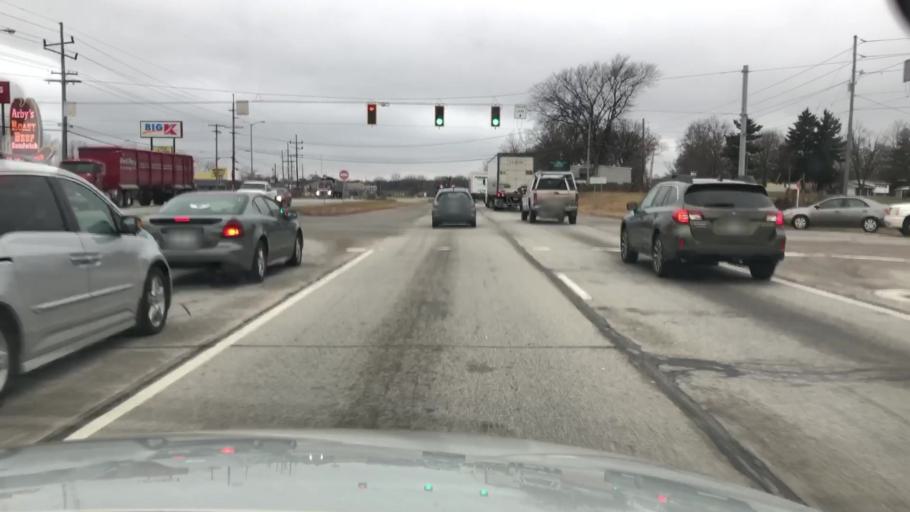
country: US
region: Indiana
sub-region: Kosciusko County
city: Winona Lake
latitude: 41.2344
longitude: -85.8065
